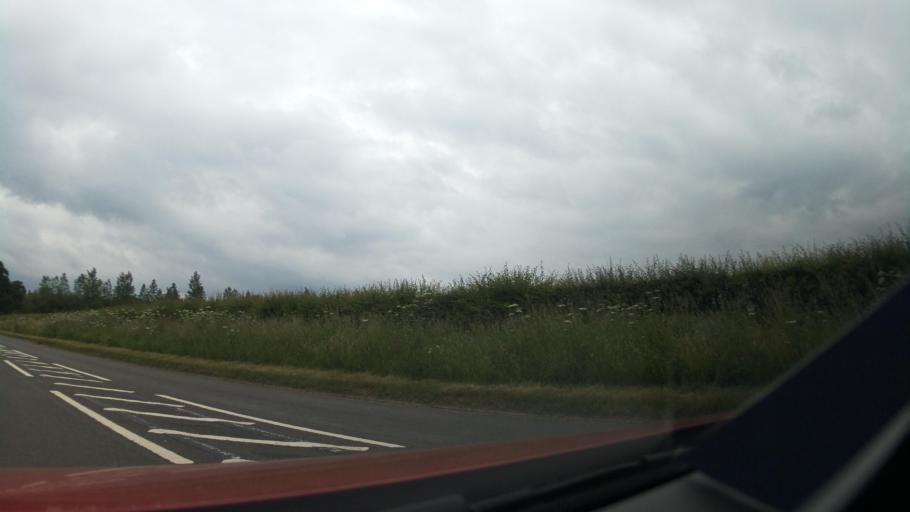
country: GB
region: England
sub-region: Staffordshire
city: Penkridge
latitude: 52.7459
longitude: -2.1076
